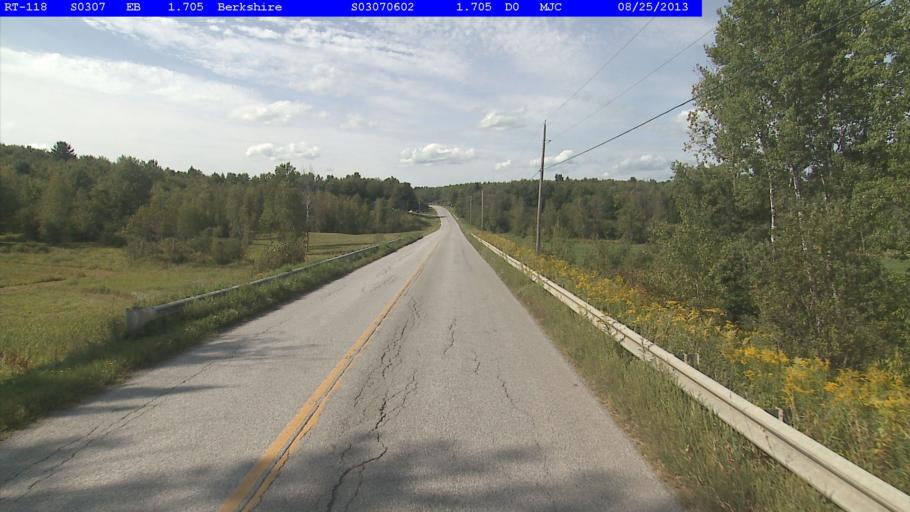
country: US
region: Vermont
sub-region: Franklin County
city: Enosburg Falls
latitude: 44.9442
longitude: -72.7407
